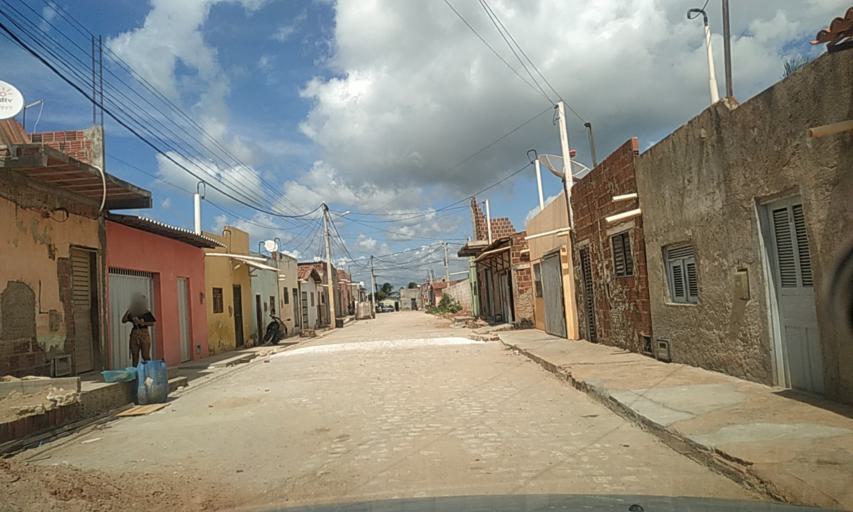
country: BR
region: Rio Grande do Norte
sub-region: Areia Branca
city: Areia Branca
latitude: -4.9520
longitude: -37.1206
